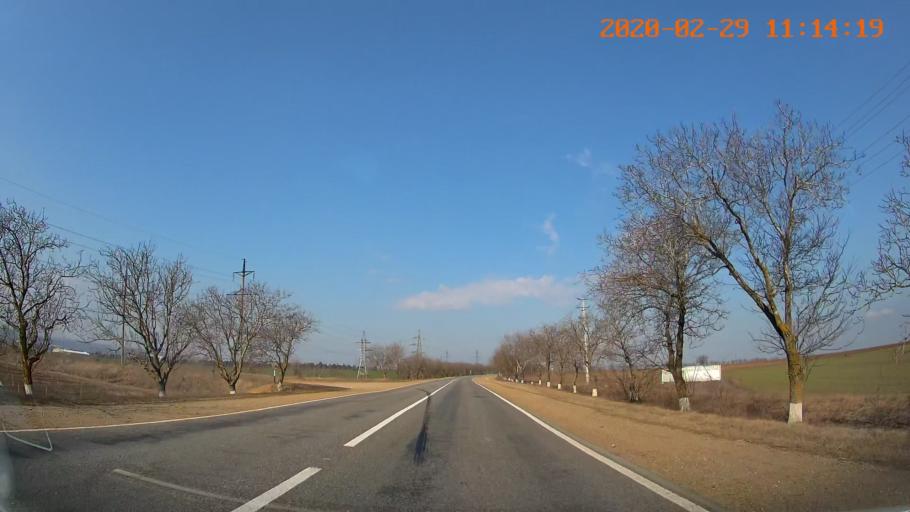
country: MD
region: Telenesti
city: Dubasari
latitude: 47.2810
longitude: 29.1731
